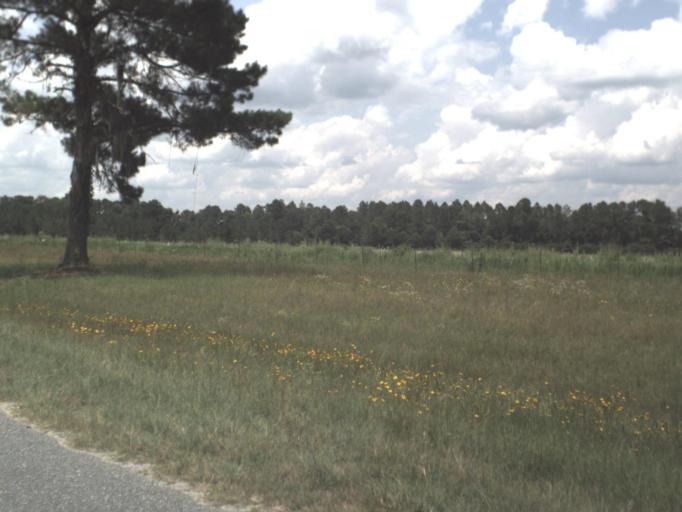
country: US
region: Georgia
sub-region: Echols County
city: Statenville
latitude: 30.5930
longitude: -83.0936
